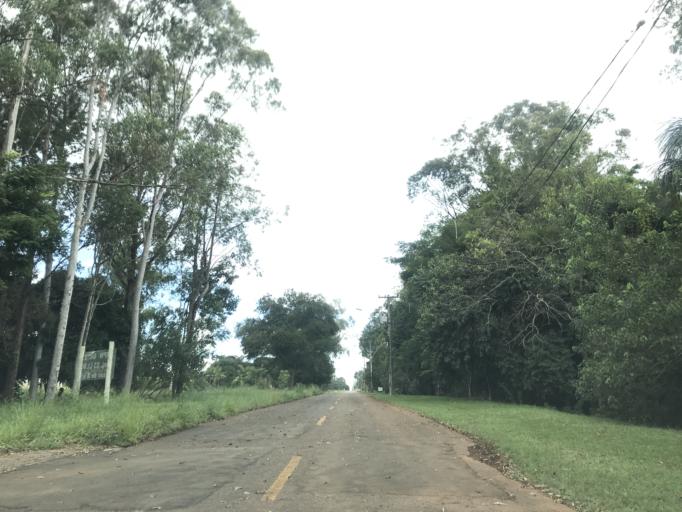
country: BR
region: Federal District
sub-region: Brasilia
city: Brasilia
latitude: -15.8864
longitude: -47.9240
